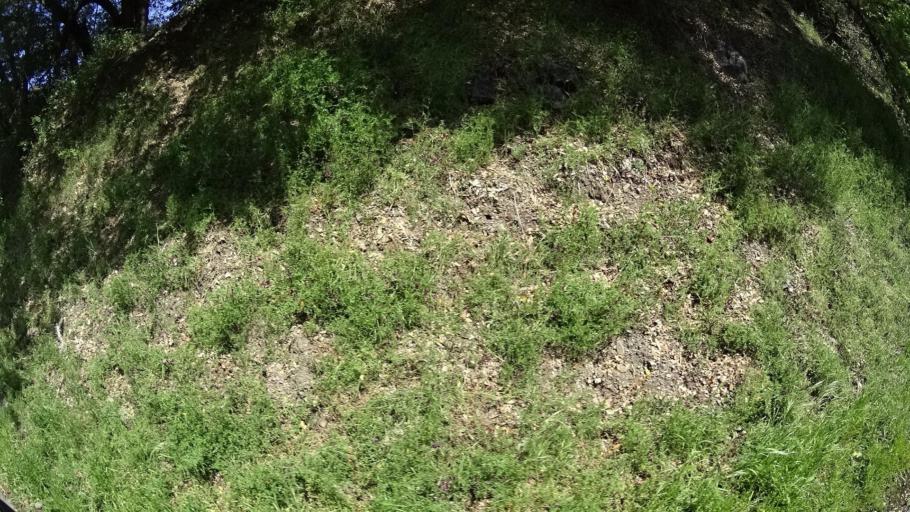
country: US
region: California
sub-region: Humboldt County
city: Redway
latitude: 40.2203
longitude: -123.6009
